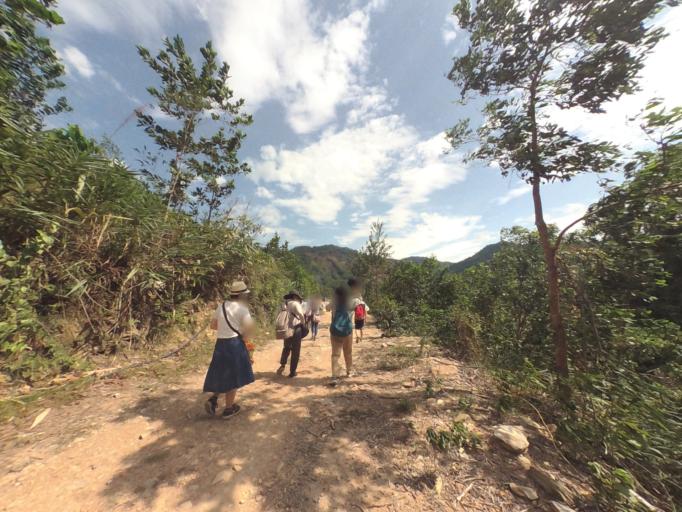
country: VN
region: Thua Thien-Hue
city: A Luoi
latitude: 16.3026
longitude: 107.3250
